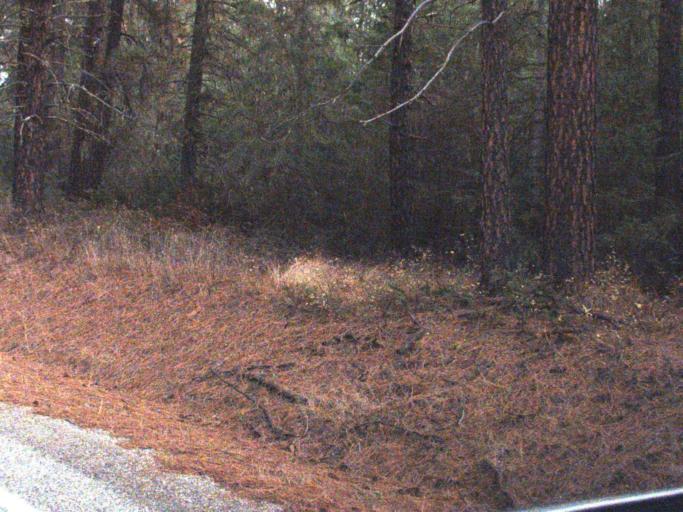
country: CA
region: British Columbia
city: Grand Forks
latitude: 48.9102
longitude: -118.2051
